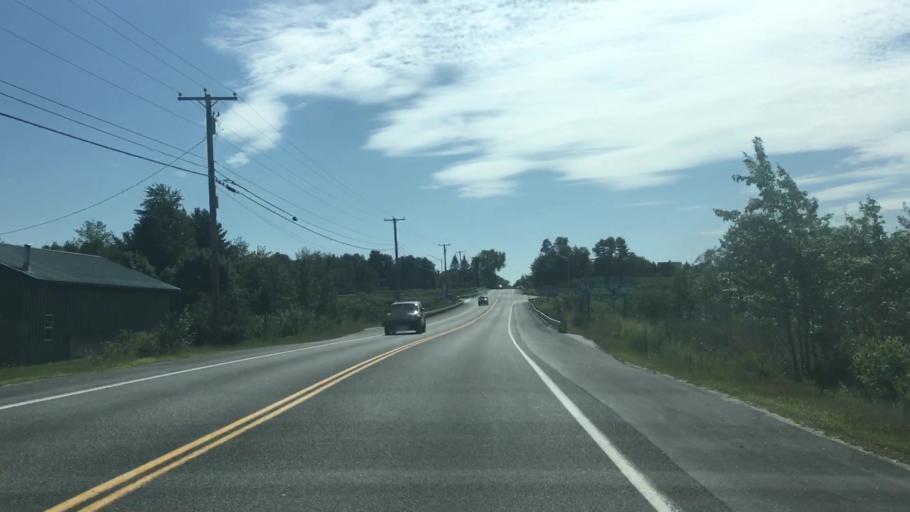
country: US
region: Maine
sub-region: Androscoggin County
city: Sabattus
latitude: 44.1036
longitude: -70.0869
